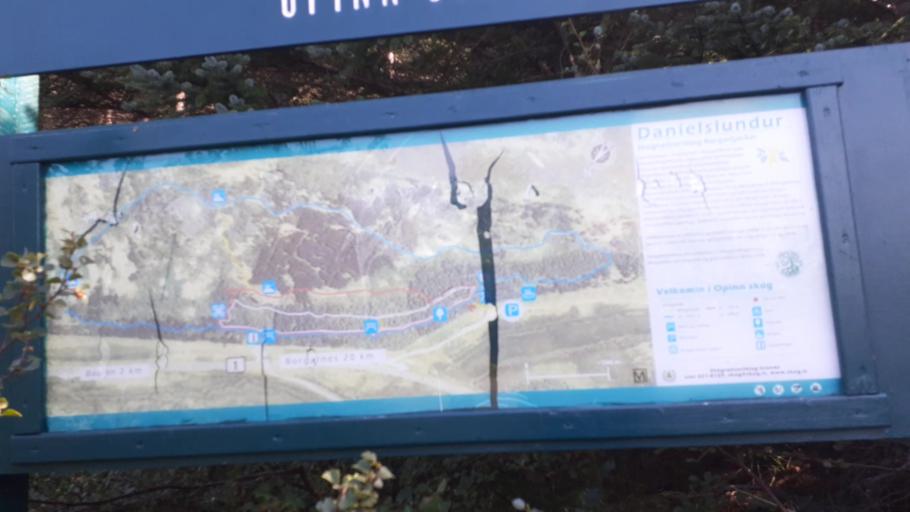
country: IS
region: West
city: Borgarnes
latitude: 64.6583
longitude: -21.7110
